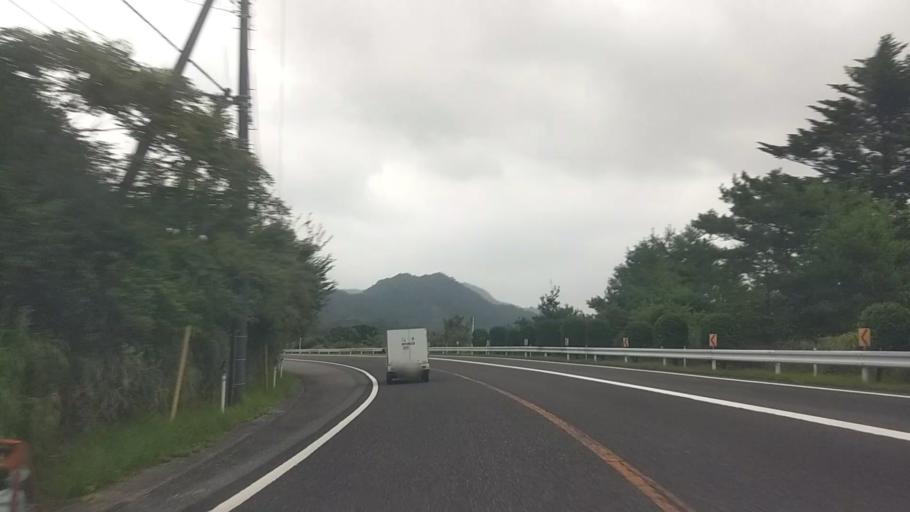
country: JP
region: Chiba
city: Kawaguchi
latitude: 35.1622
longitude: 140.0621
